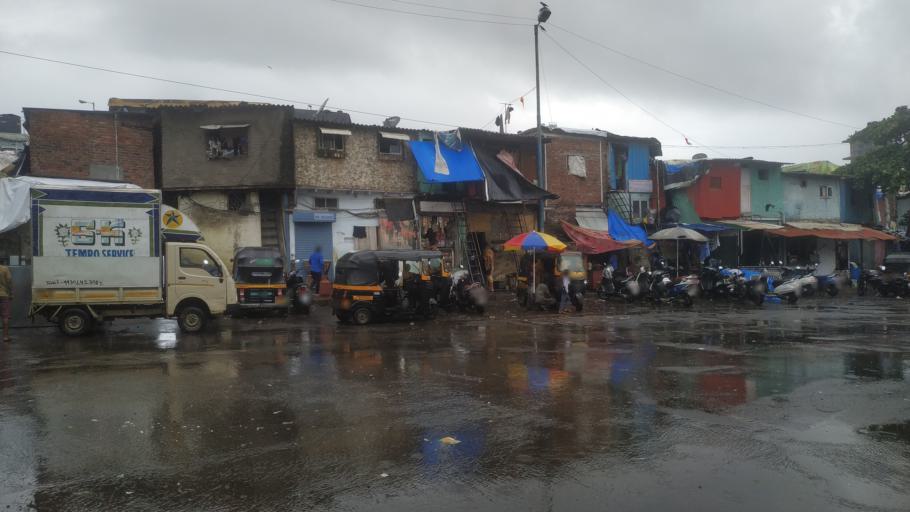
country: IN
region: Maharashtra
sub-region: Mumbai Suburban
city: Mumbai
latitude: 19.0503
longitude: 72.8369
